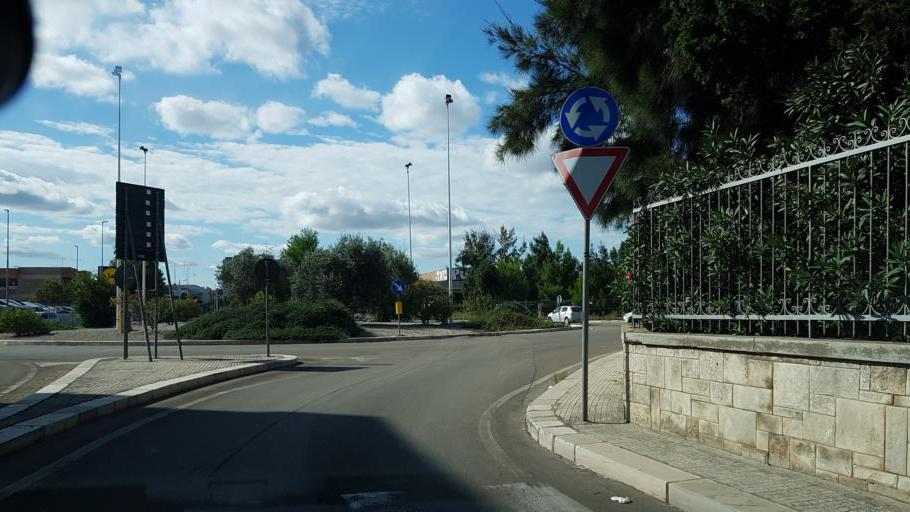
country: IT
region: Apulia
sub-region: Provincia di Lecce
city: Lecce
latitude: 40.3610
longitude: 18.1571
